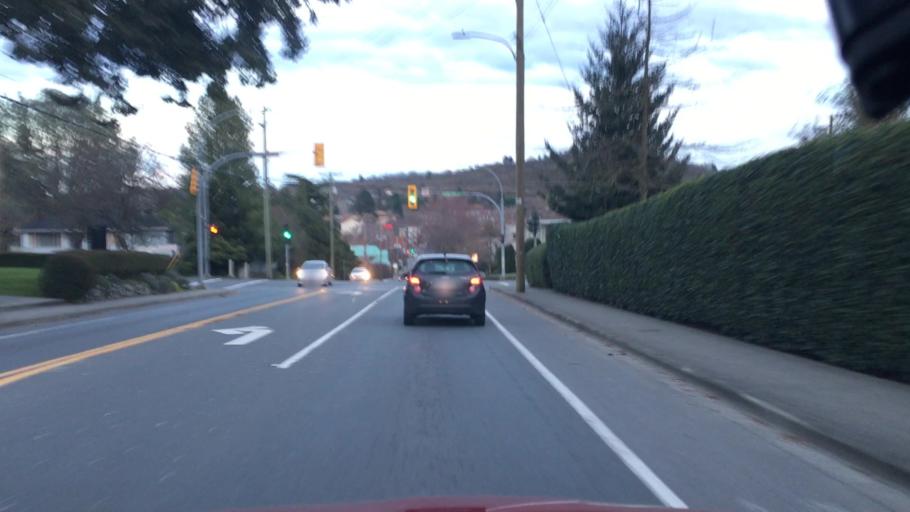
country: CA
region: British Columbia
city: Oak Bay
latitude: 48.4629
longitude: -123.3377
